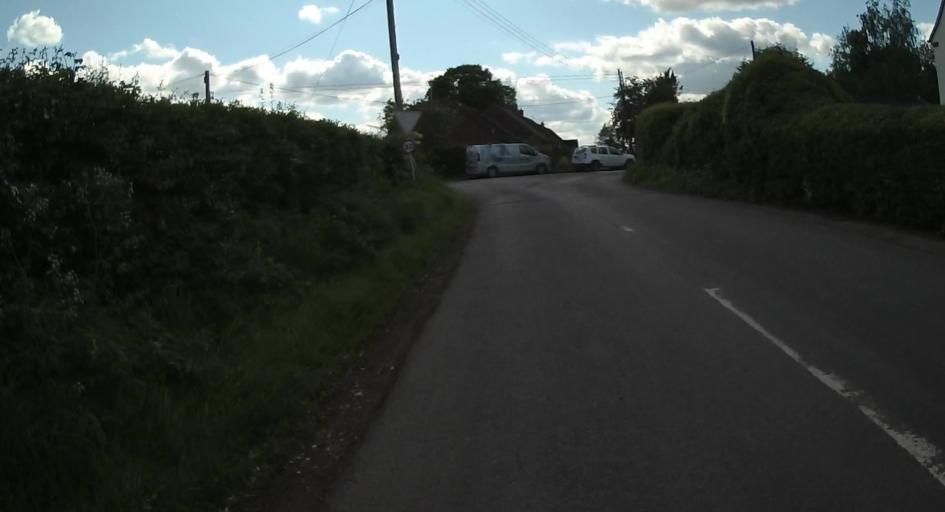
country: GB
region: England
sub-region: West Berkshire
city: Stratfield Mortimer
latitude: 51.3495
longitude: -1.0422
